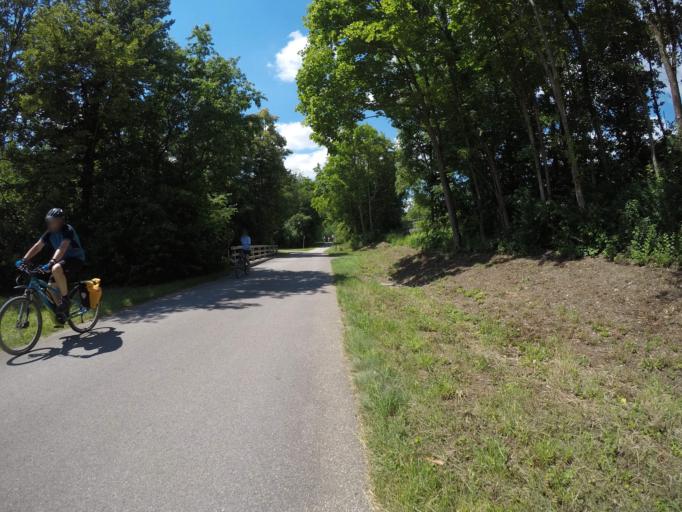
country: DE
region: Bavaria
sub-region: Lower Bavaria
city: Essing
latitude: 48.9303
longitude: 11.7926
